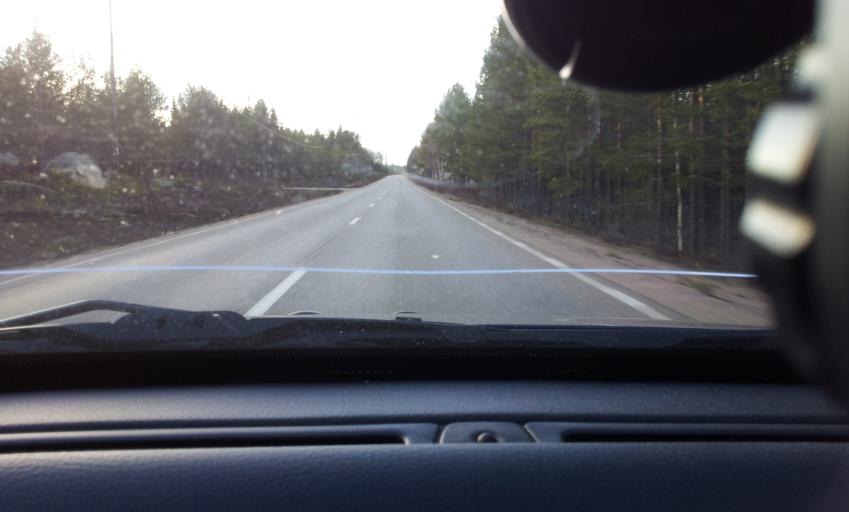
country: SE
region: Jaemtland
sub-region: Harjedalens Kommun
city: Sveg
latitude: 62.0965
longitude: 15.0810
